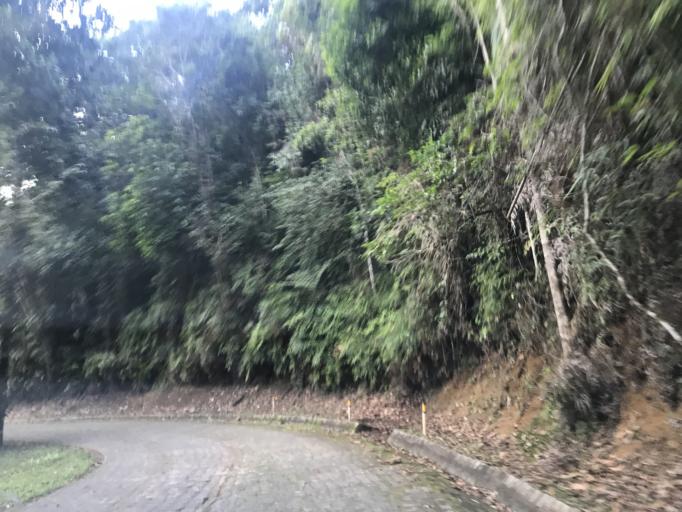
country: BR
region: Bahia
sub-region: Gandu
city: Gandu
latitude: -13.9114
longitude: -39.4638
